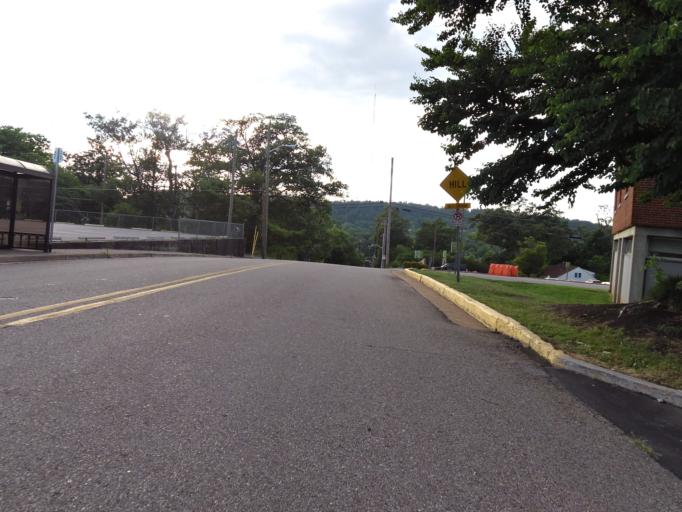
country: US
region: Tennessee
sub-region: Knox County
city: Knoxville
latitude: 35.9923
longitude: -83.9282
